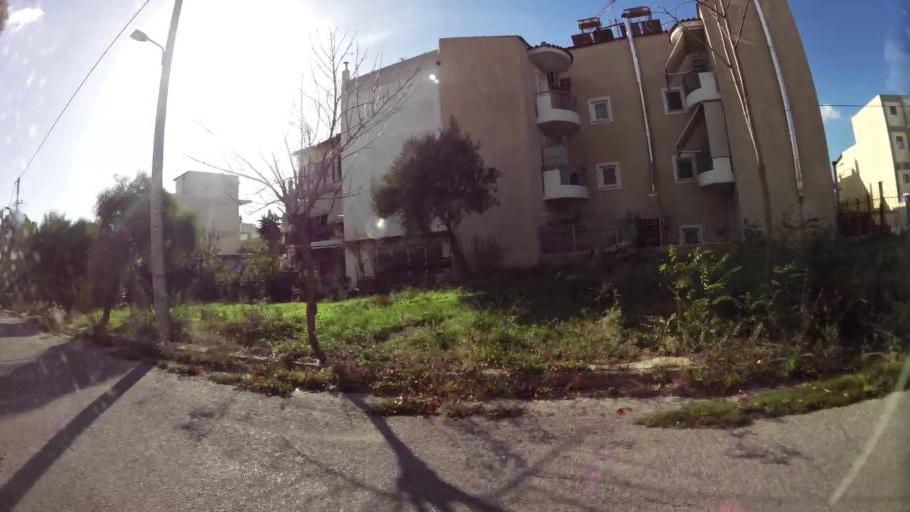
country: GR
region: Attica
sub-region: Nomarchia Anatolikis Attikis
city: Acharnes
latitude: 38.0679
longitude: 23.7421
